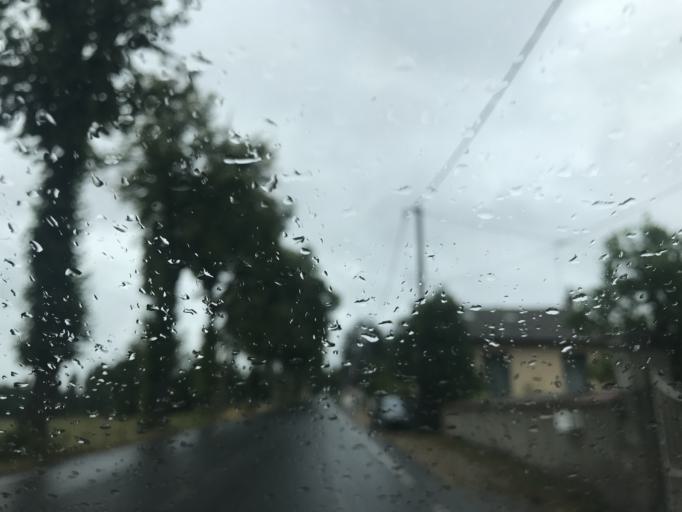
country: FR
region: Auvergne
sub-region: Departement du Puy-de-Dome
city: Ambert
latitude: 45.5562
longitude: 3.7411
